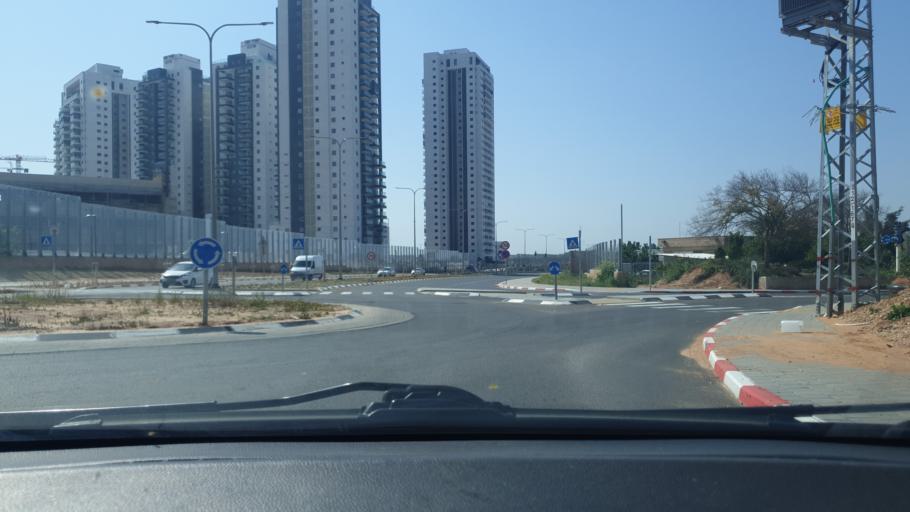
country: IL
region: Central District
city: Ramla
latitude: 31.9357
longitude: 34.8515
